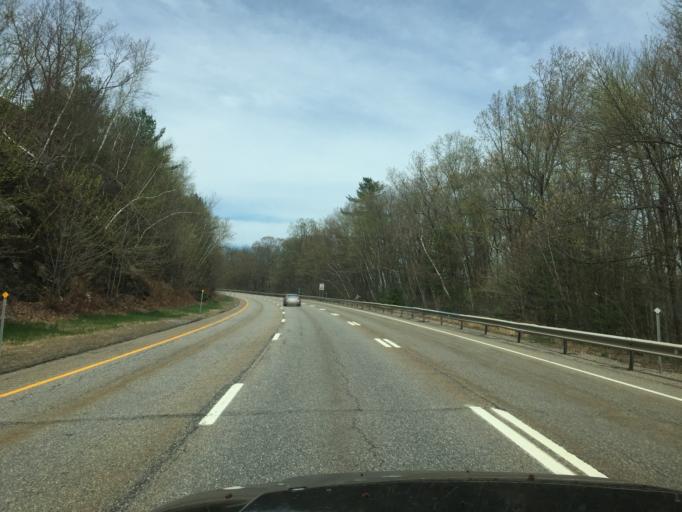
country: US
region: Connecticut
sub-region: Litchfield County
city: Thomaston
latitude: 41.7016
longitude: -73.0705
